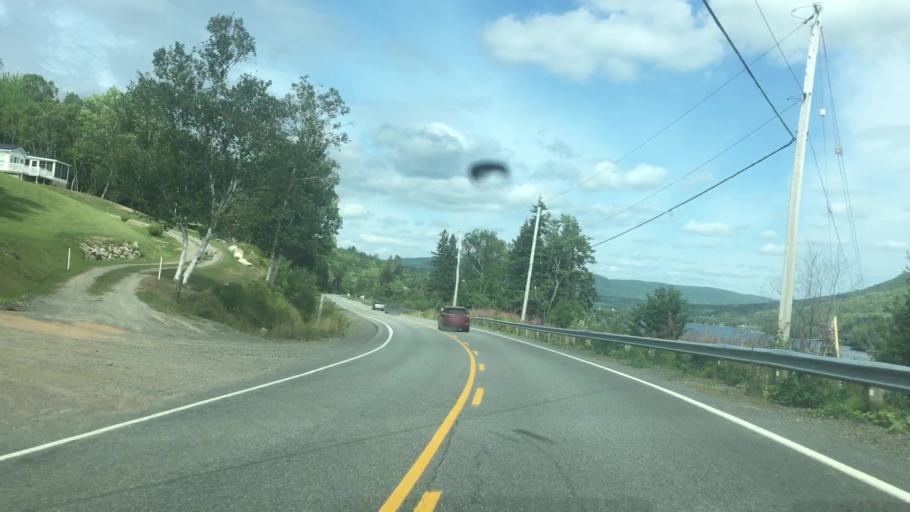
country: CA
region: Nova Scotia
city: Sydney Mines
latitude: 46.2725
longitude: -60.6096
